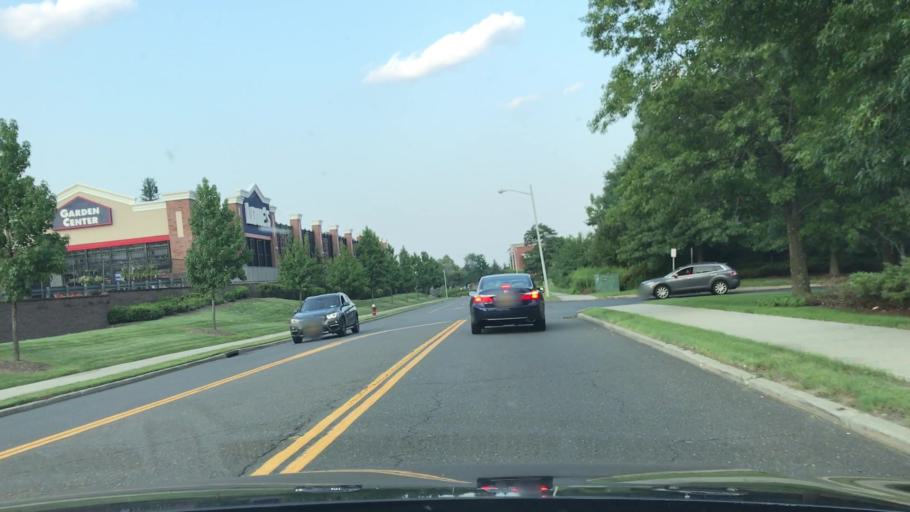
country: US
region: New York
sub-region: Rockland County
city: Spring Valley
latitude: 41.1083
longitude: -74.0250
